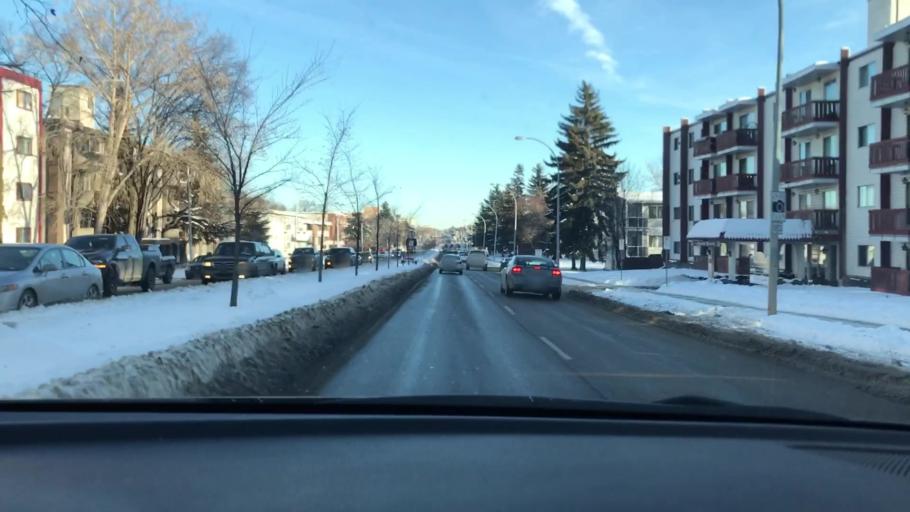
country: CA
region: Alberta
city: Edmonton
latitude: 53.5180
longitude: -113.4845
